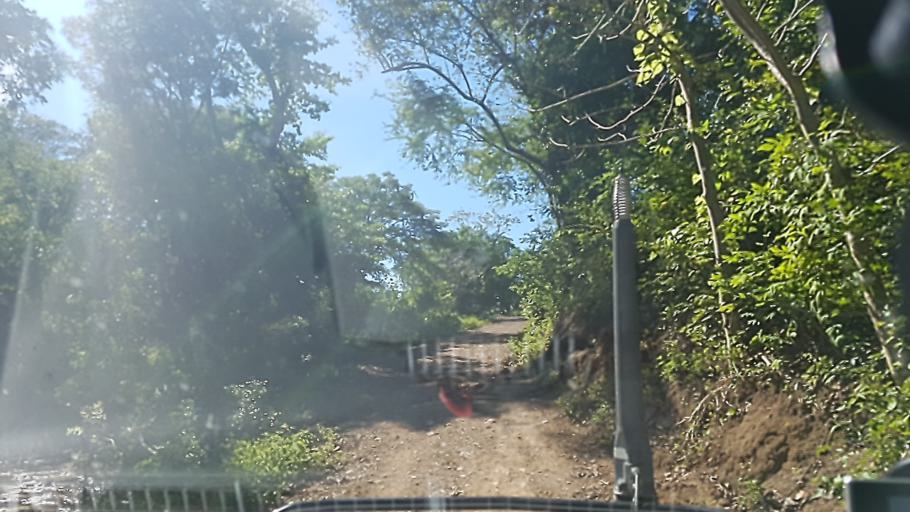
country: NI
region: Rivas
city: Tola
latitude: 11.5423
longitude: -86.1026
